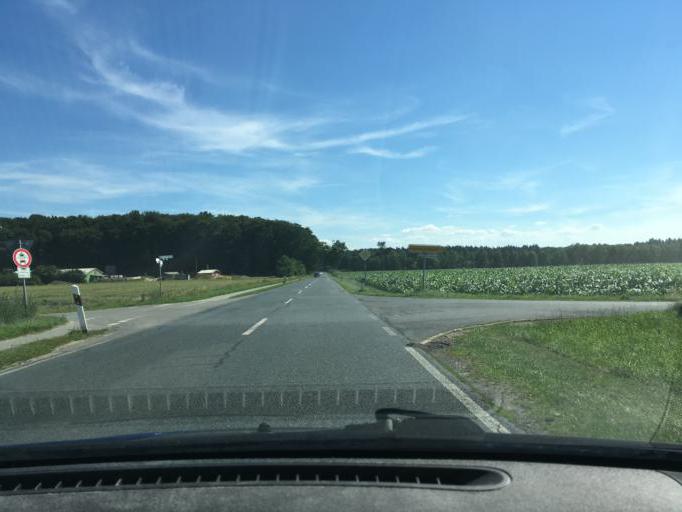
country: DE
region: Lower Saxony
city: Bendestorf
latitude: 53.3566
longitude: 9.9413
